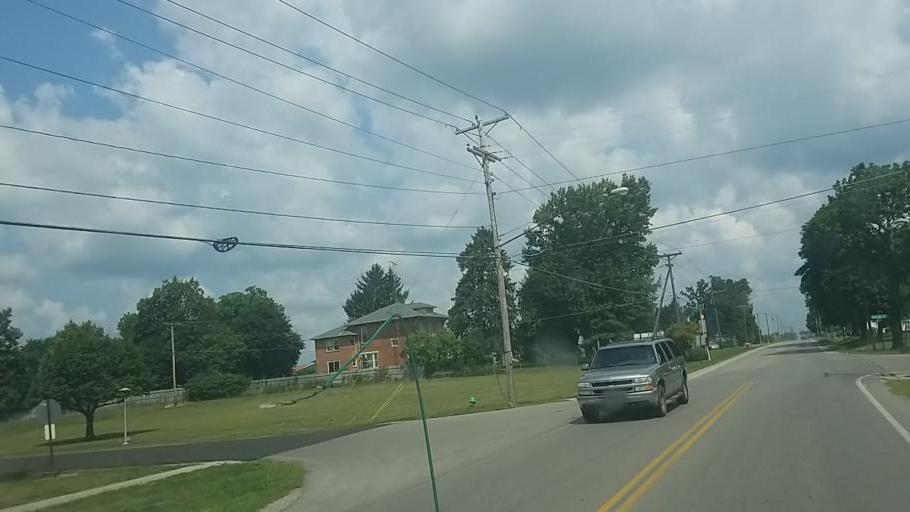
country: US
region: Ohio
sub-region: Wyandot County
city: Upper Sandusky
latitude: 40.8418
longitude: -83.2807
